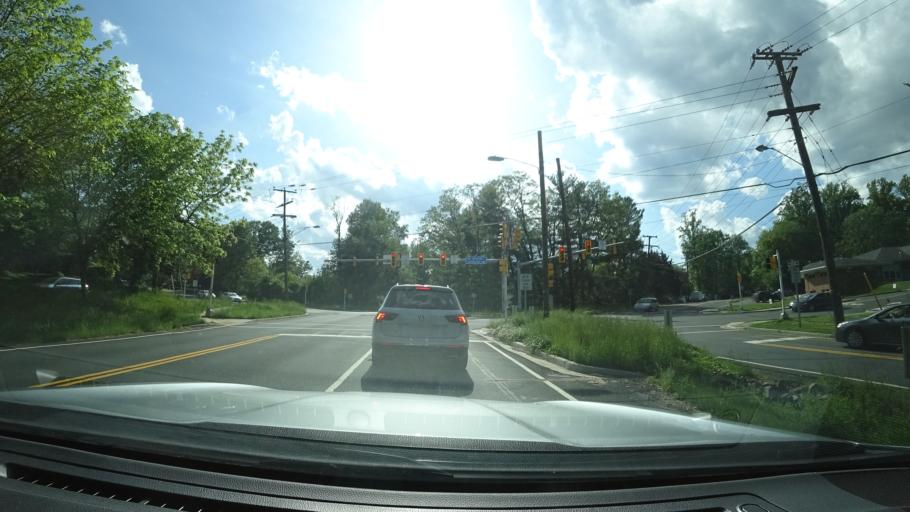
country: US
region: Virginia
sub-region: Fairfax County
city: McLean
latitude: 38.9242
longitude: -77.1612
